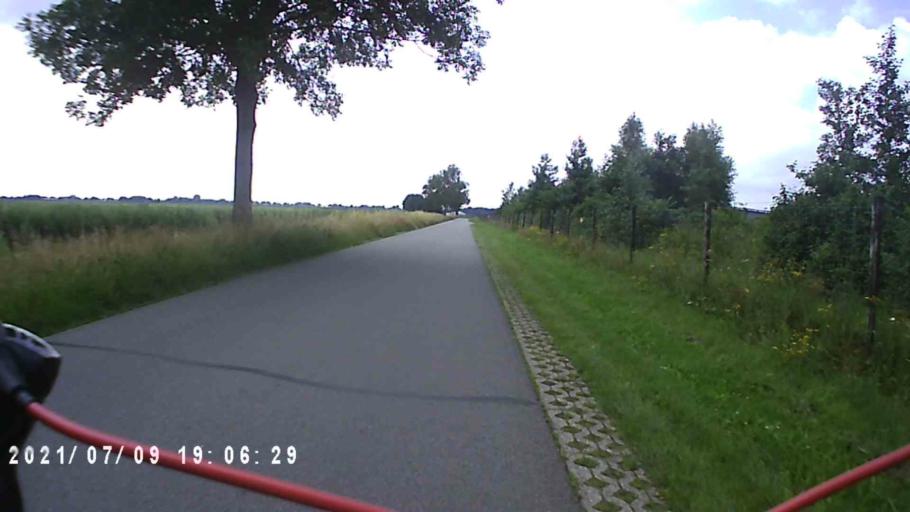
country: NL
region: Groningen
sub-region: Gemeente Veendam
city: Veendam
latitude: 53.0573
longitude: 6.8794
